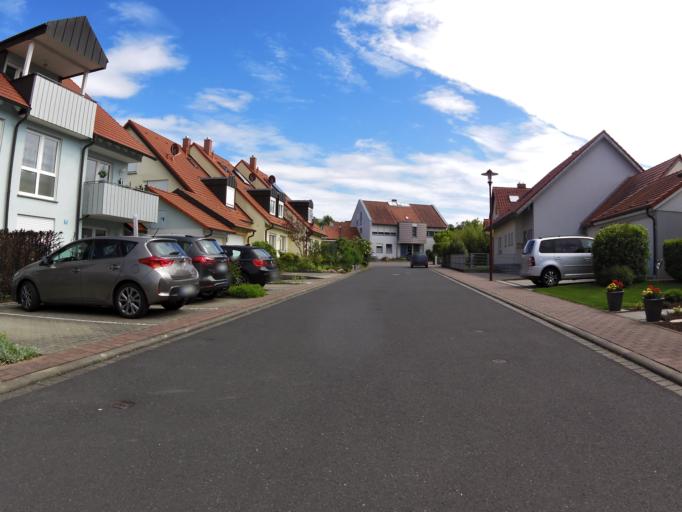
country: DE
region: Bavaria
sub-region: Regierungsbezirk Unterfranken
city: Kurnach
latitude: 49.8414
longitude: 10.0422
